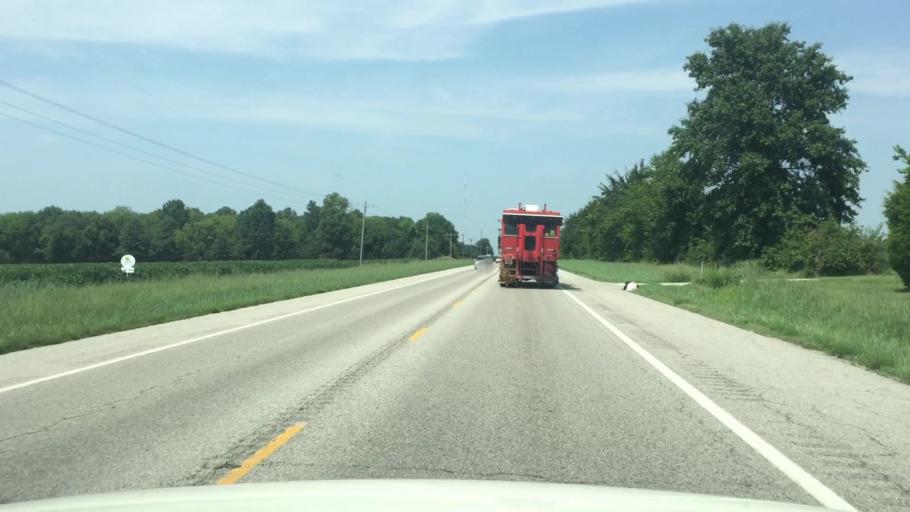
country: US
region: Kansas
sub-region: Cherokee County
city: Galena
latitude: 37.1892
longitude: -94.7046
